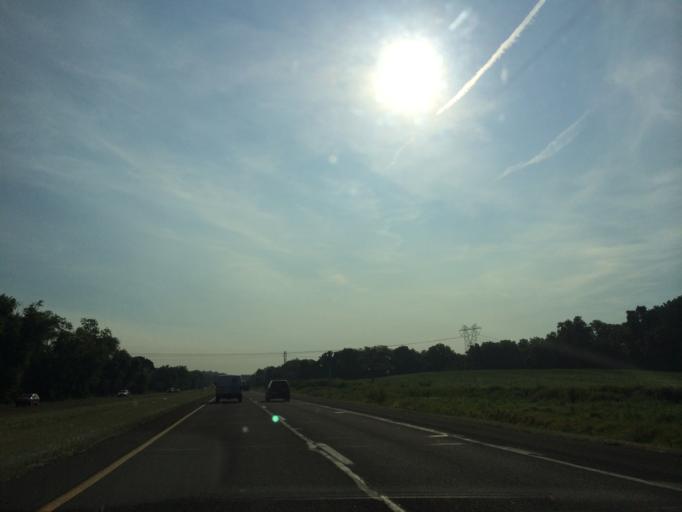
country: US
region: Pennsylvania
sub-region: York County
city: Yorklyn
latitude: 40.0006
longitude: -76.6339
